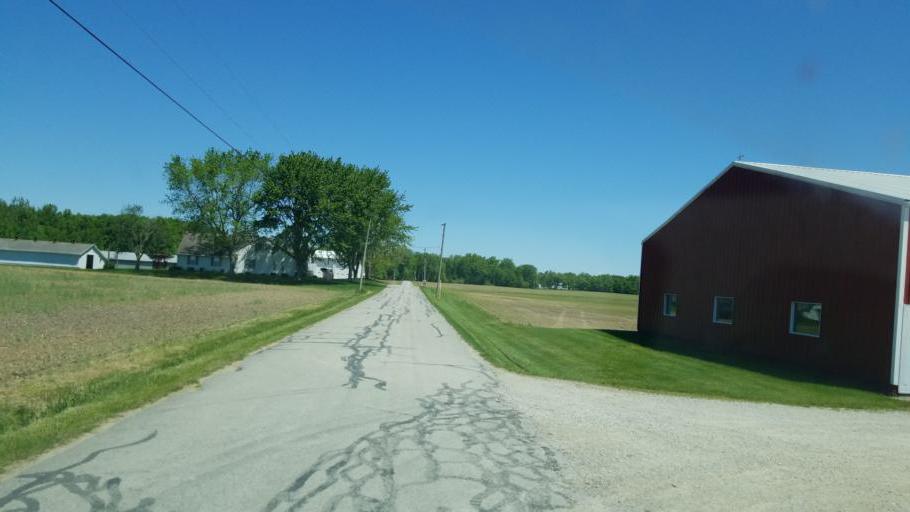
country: US
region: Ohio
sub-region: Shelby County
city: Fort Loramie
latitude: 40.3733
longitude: -84.3165
